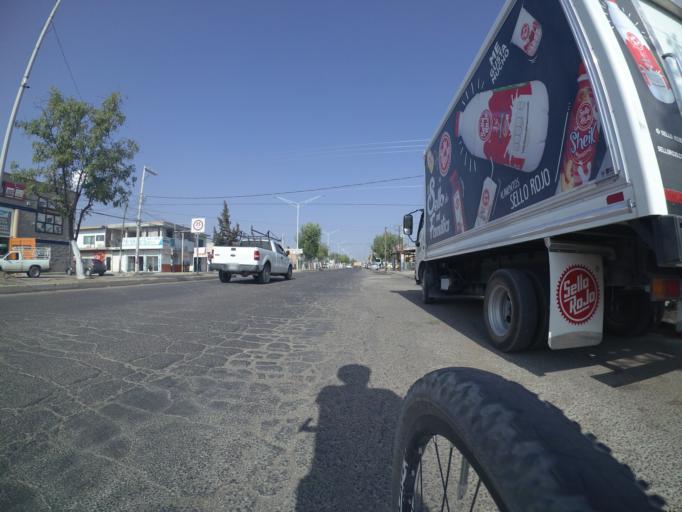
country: MX
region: Aguascalientes
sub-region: Jesus Maria
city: Tepetates
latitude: 21.9509
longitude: -102.3251
